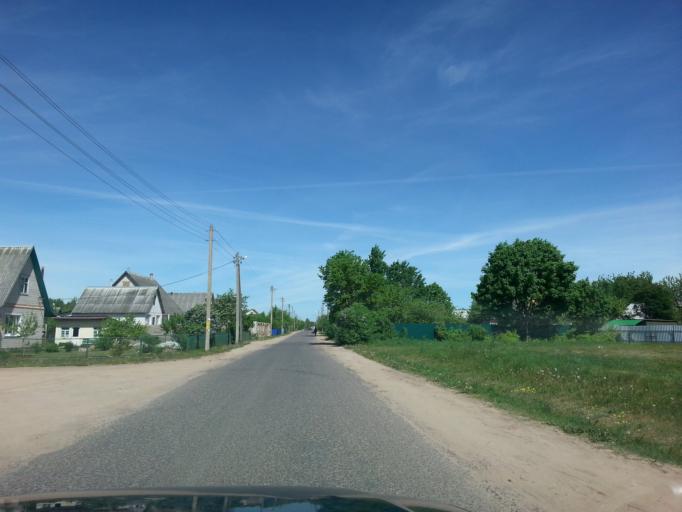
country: BY
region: Minsk
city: Narach
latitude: 54.9265
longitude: 26.6912
